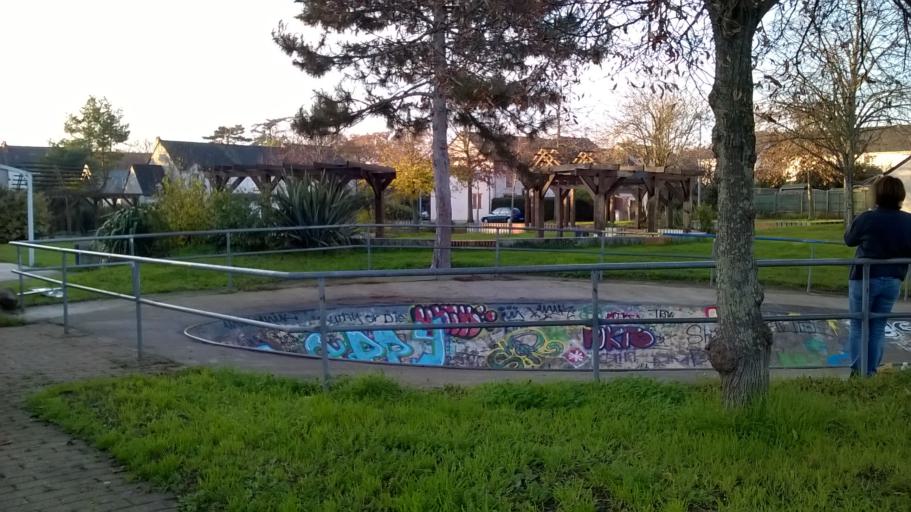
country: FR
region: Pays de la Loire
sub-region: Departement de la Loire-Atlantique
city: Bouguenais
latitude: 47.2007
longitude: -1.5923
